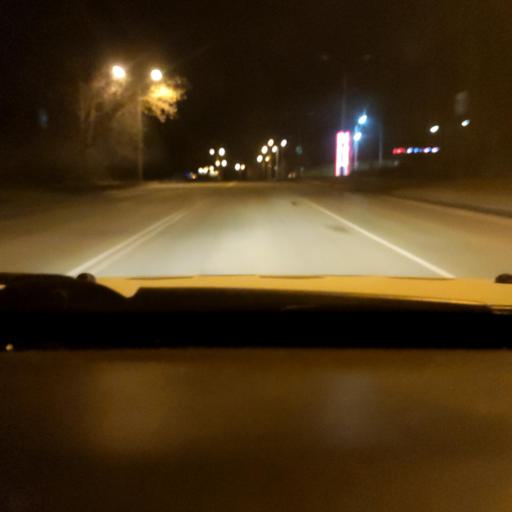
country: RU
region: Perm
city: Perm
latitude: 58.0640
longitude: 56.3637
